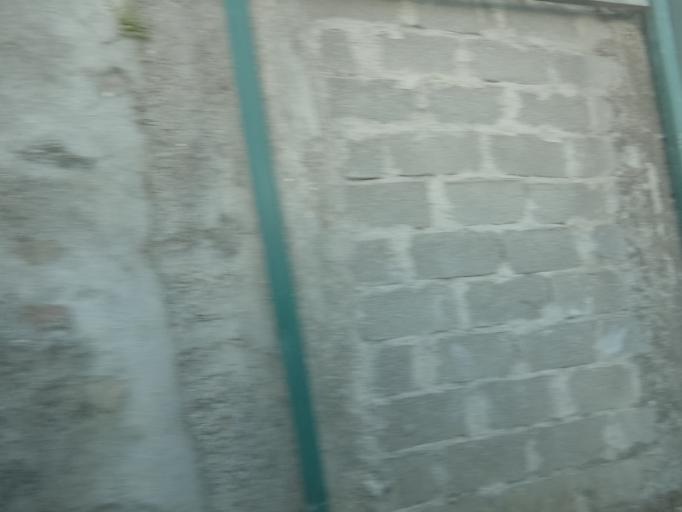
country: PT
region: Vila Real
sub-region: Peso da Regua
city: Godim
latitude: 41.1600
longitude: -7.8104
